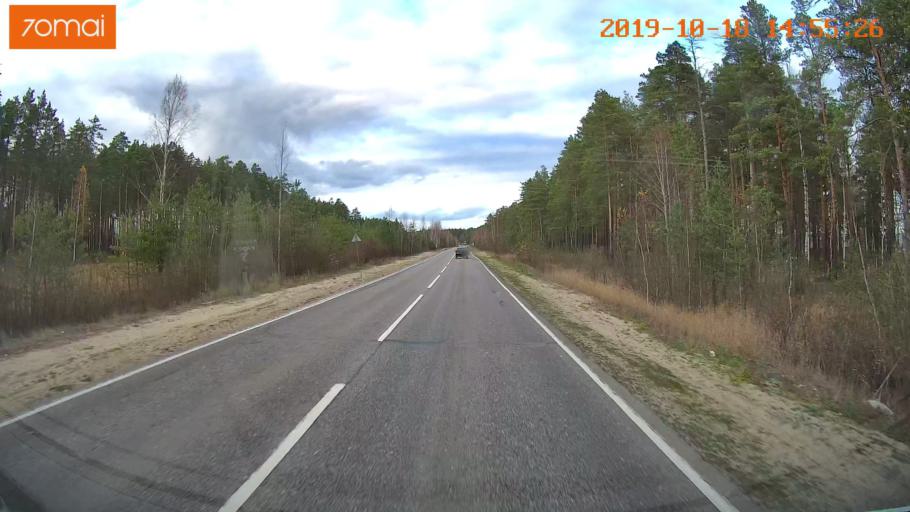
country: RU
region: Vladimir
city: Kurlovo
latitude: 55.4521
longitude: 40.5888
